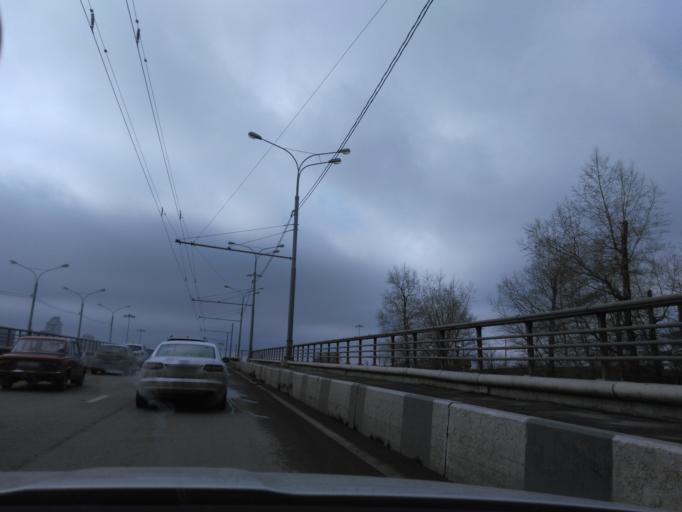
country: RU
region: Moscow
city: Pokrovskoye-Streshnevo
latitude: 55.8226
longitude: 37.4505
